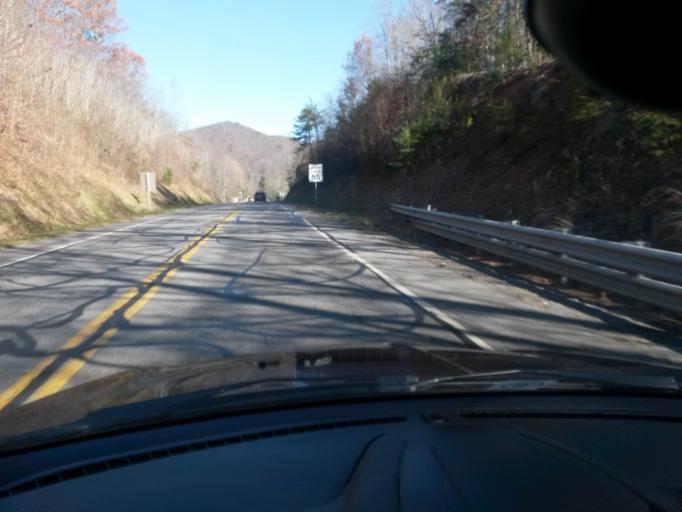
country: US
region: Virginia
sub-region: Patrick County
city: Stuart
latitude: 36.6614
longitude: -80.2757
